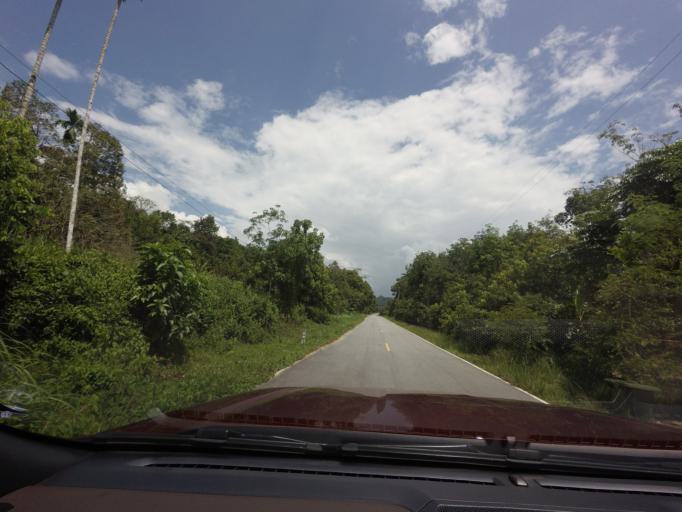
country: TH
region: Narathiwat
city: Chanae
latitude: 6.0805
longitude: 101.6890
